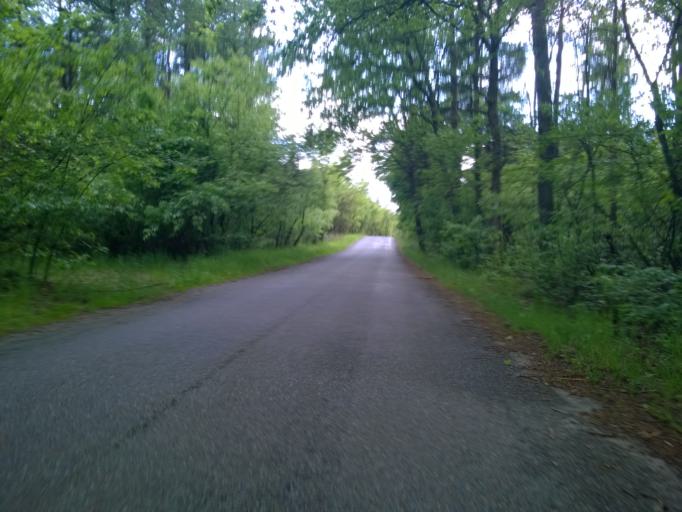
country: DK
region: Central Jutland
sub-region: Holstebro Kommune
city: Vinderup
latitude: 56.5154
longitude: 8.8421
